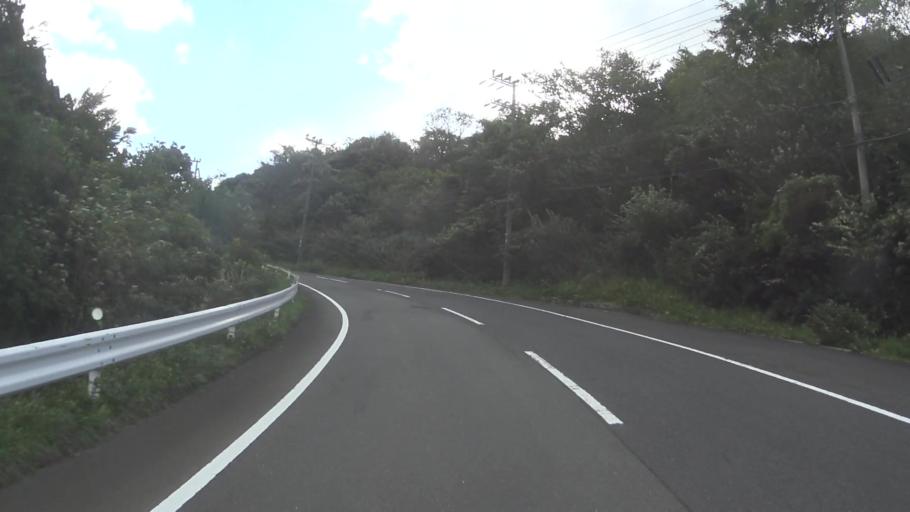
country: JP
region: Kyoto
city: Maizuru
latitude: 35.5409
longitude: 135.3977
